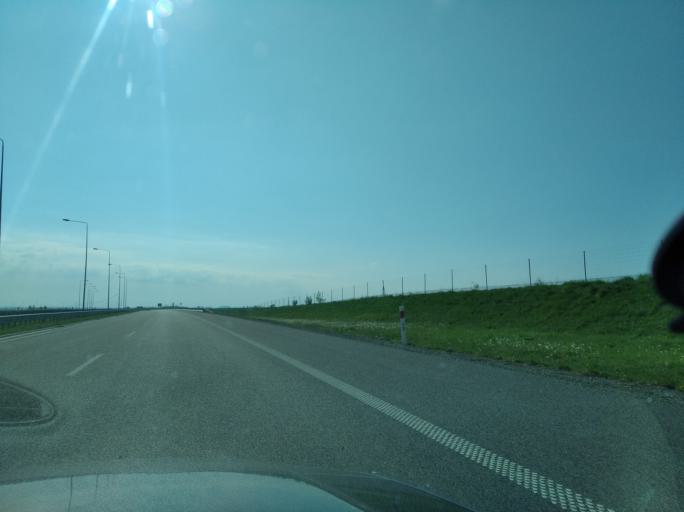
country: PL
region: Subcarpathian Voivodeship
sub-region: Powiat jaroslawski
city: Ostrow
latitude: 49.9187
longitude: 22.7438
